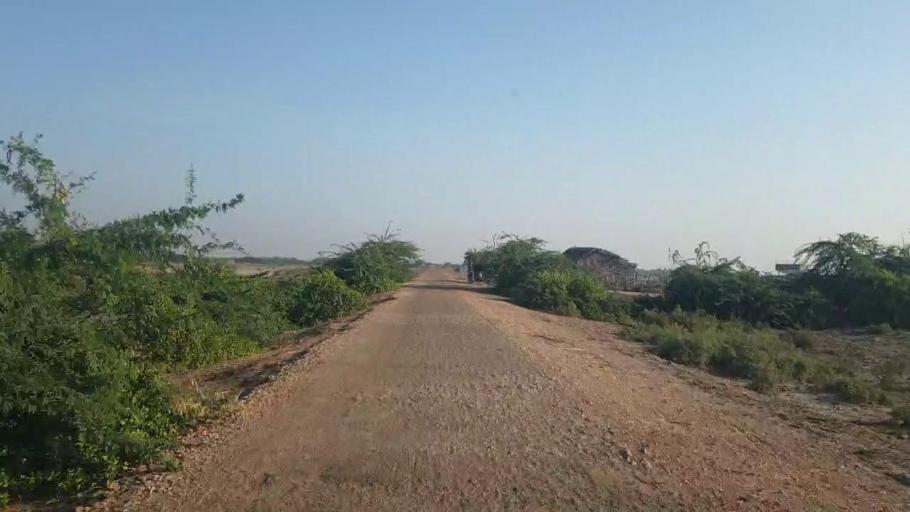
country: PK
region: Sindh
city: Badin
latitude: 24.7253
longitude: 68.8643
